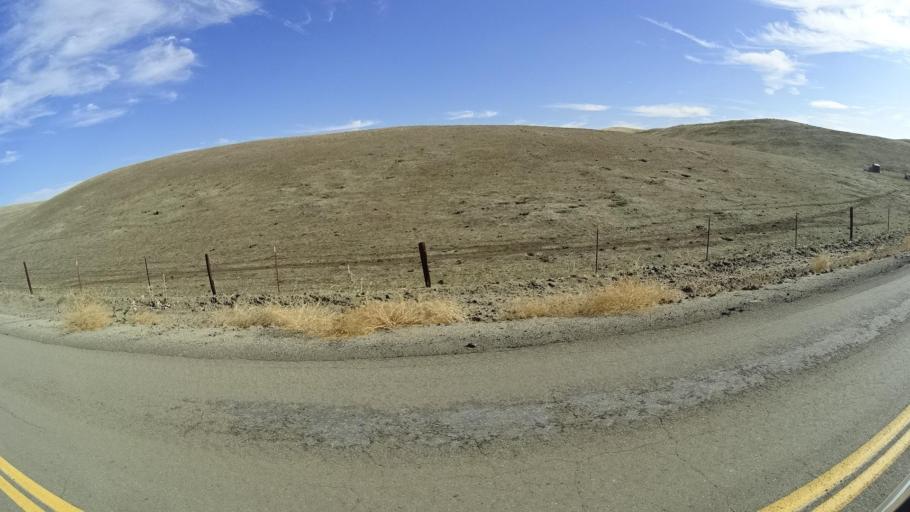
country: US
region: California
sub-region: Kern County
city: Oildale
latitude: 35.6105
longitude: -118.9442
